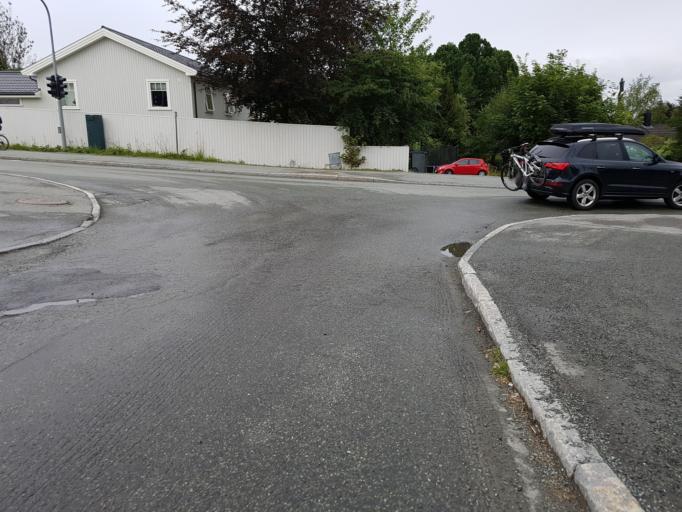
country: NO
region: Sor-Trondelag
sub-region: Trondheim
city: Trondheim
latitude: 63.3996
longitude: 10.3726
